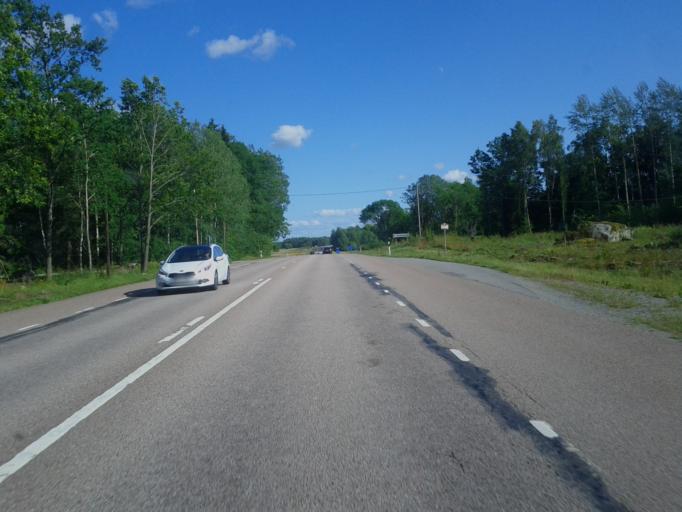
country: SE
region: Uppsala
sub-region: Enkopings Kommun
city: Enkoping
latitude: 59.6737
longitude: 17.0556
